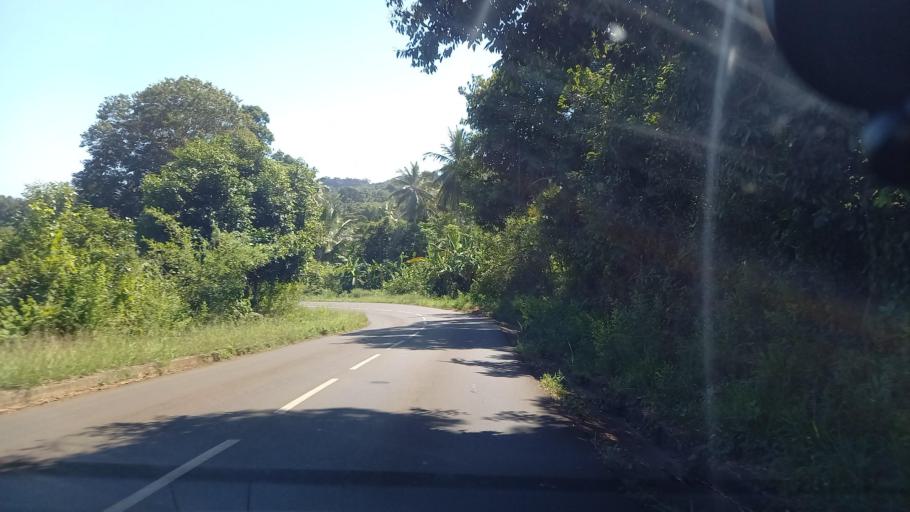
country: YT
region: Tsingoni
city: Tsingoni
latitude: -12.7847
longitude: 45.1430
